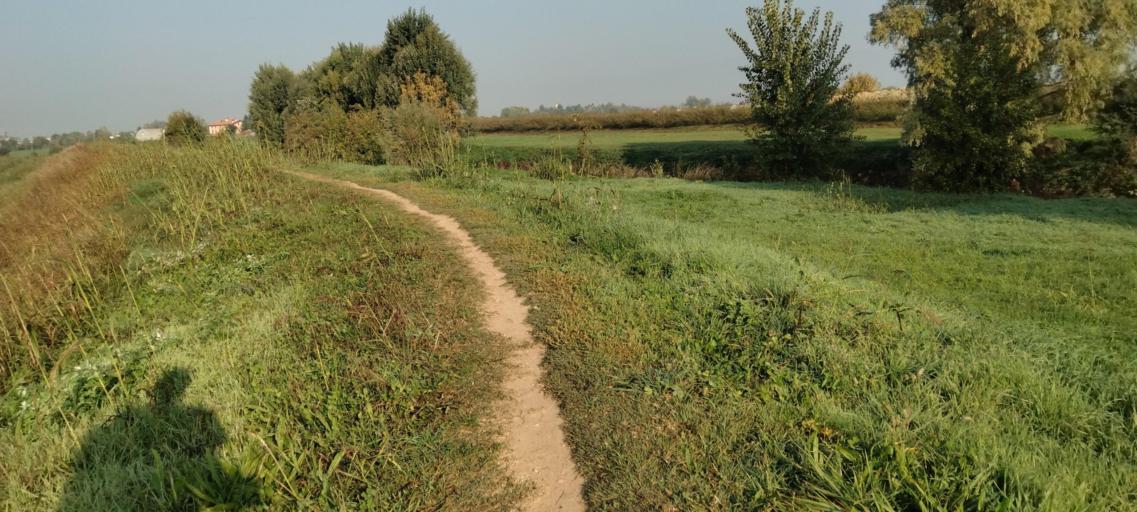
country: IT
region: Veneto
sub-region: Provincia di Vicenza
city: Monticello Conte Otto
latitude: 45.5908
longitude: 11.5409
